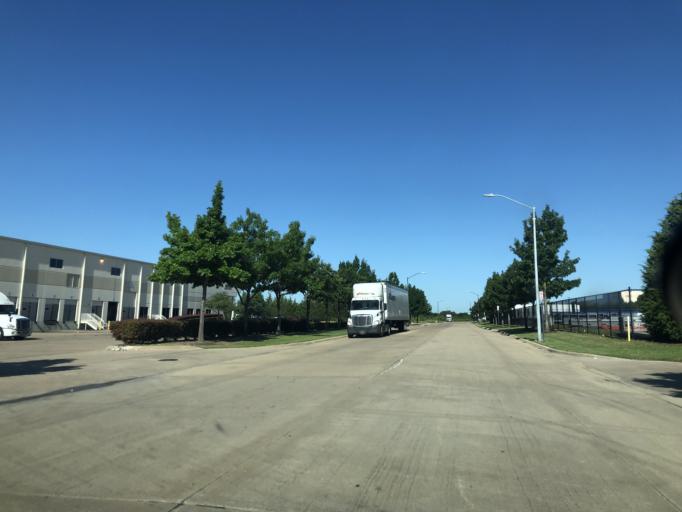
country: US
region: Texas
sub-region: Tarrant County
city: Euless
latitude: 32.8097
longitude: -97.0368
